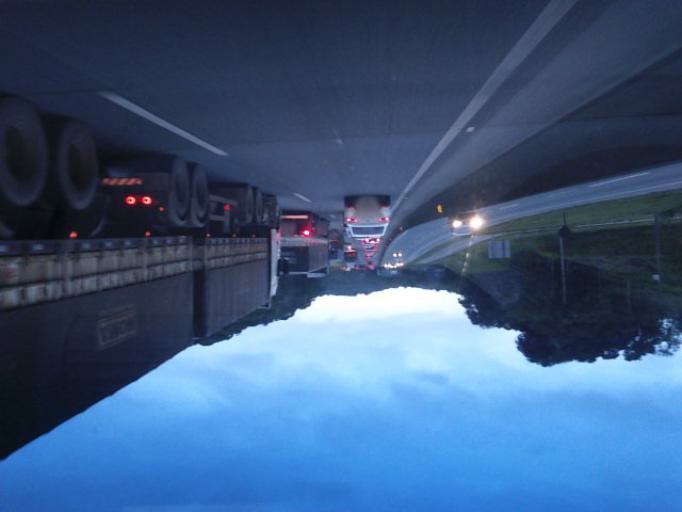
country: BR
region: Santa Catarina
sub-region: Joinville
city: Joinville
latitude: -26.3758
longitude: -48.8544
